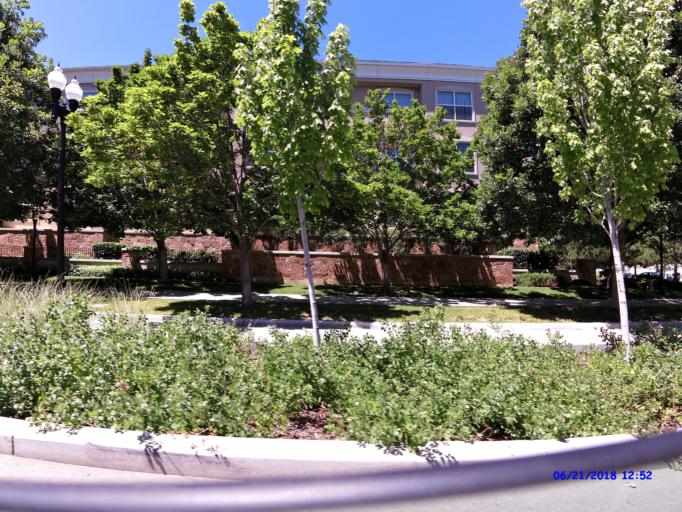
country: US
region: Utah
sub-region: Weber County
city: Ogden
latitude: 41.2287
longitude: -111.9732
